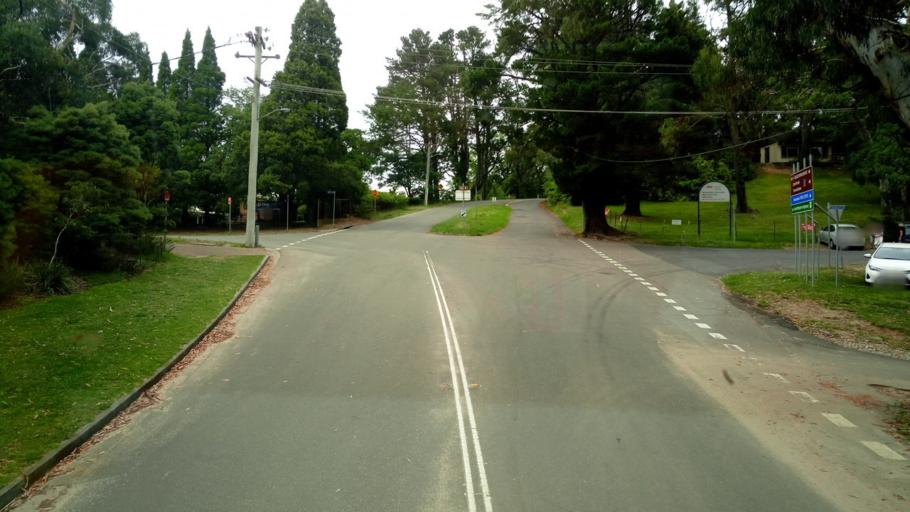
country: AU
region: New South Wales
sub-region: Blue Mountains Municipality
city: Katoomba
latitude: -33.7286
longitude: 150.2999
